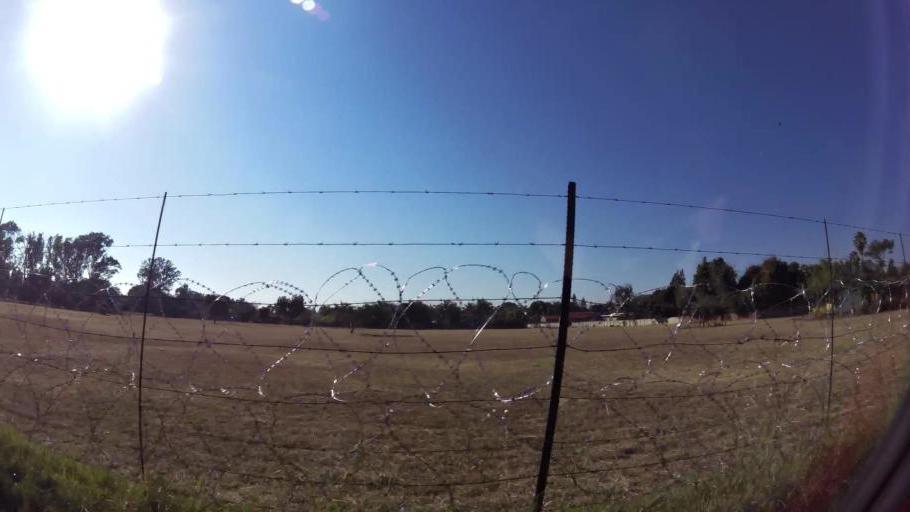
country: ZA
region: Gauteng
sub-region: City of Tshwane Metropolitan Municipality
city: Pretoria
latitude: -25.6656
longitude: 28.1429
